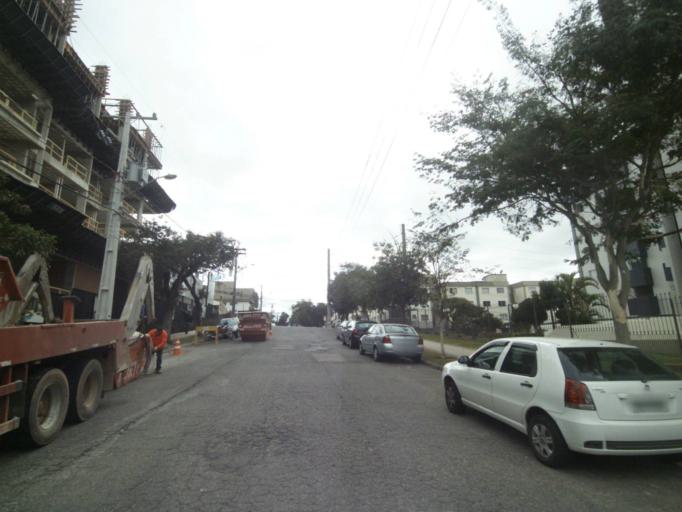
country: BR
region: Parana
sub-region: Curitiba
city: Curitiba
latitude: -25.4650
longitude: -49.2871
